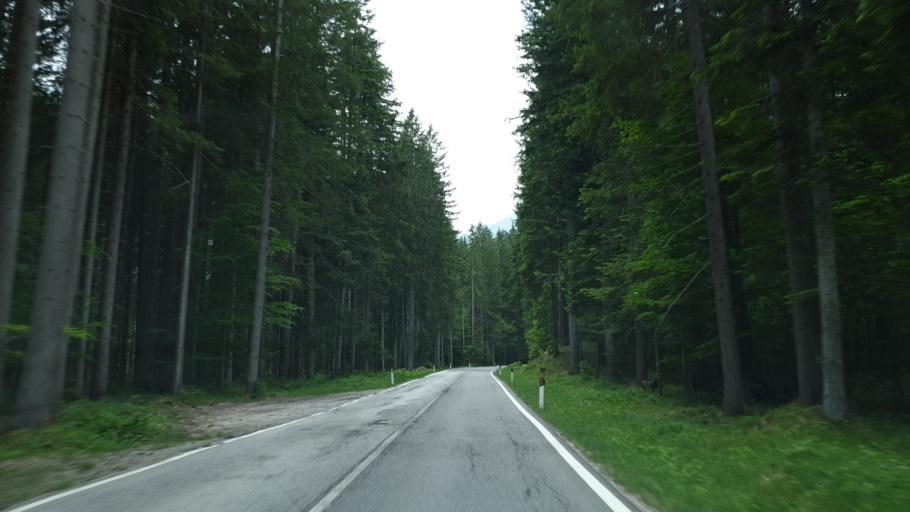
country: IT
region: Veneto
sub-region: Provincia di Belluno
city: San Vito
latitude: 46.5311
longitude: 12.2811
